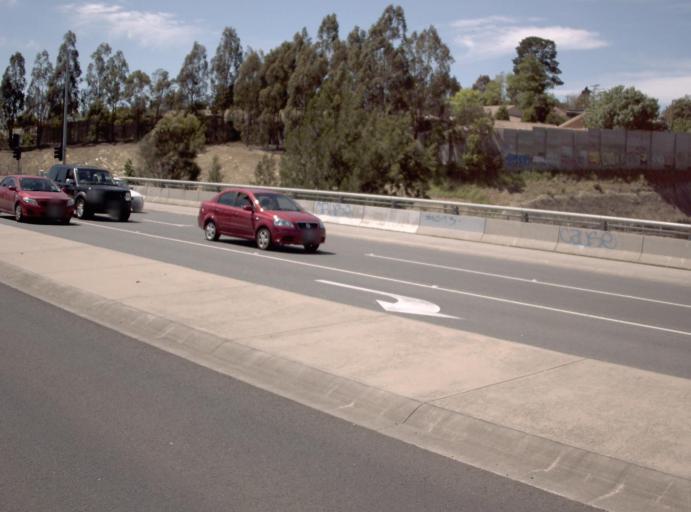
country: AU
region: Victoria
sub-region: Whitehorse
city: Blackburn North
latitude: -37.8014
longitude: 145.1596
